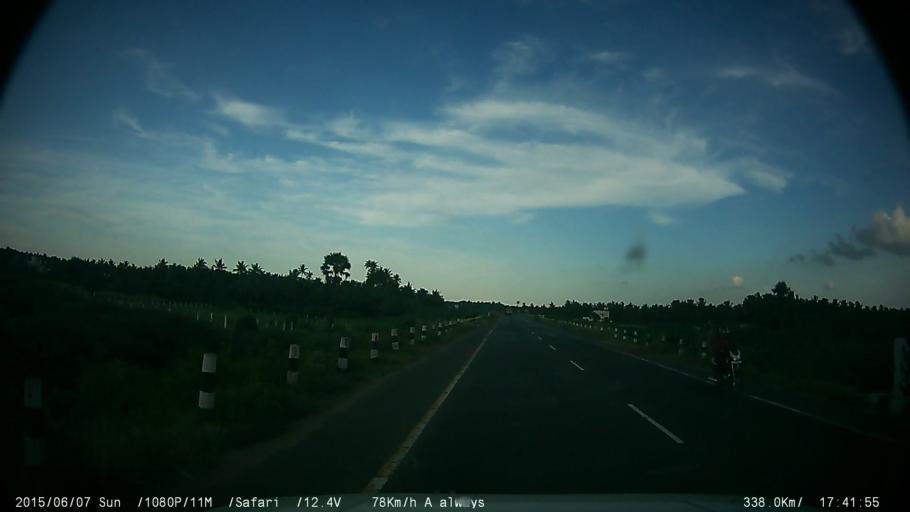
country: IN
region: Tamil Nadu
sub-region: Coimbatore
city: Madukkarai
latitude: 10.8964
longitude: 76.9604
